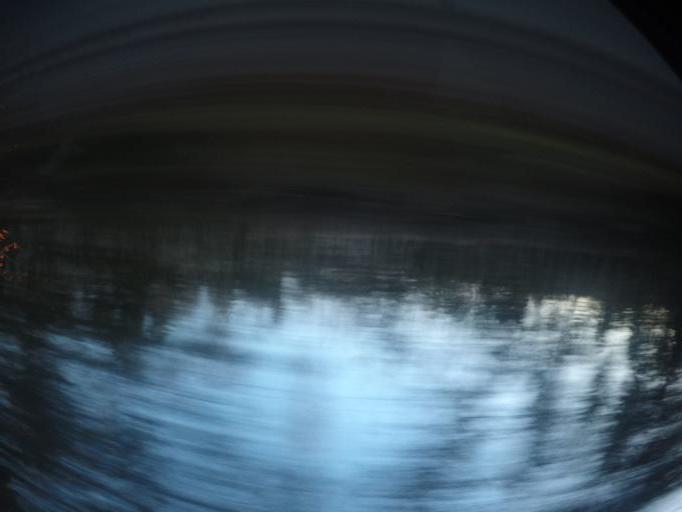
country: SE
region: OErebro
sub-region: Lindesbergs Kommun
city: Fellingsbro
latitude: 59.3397
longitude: 15.5342
